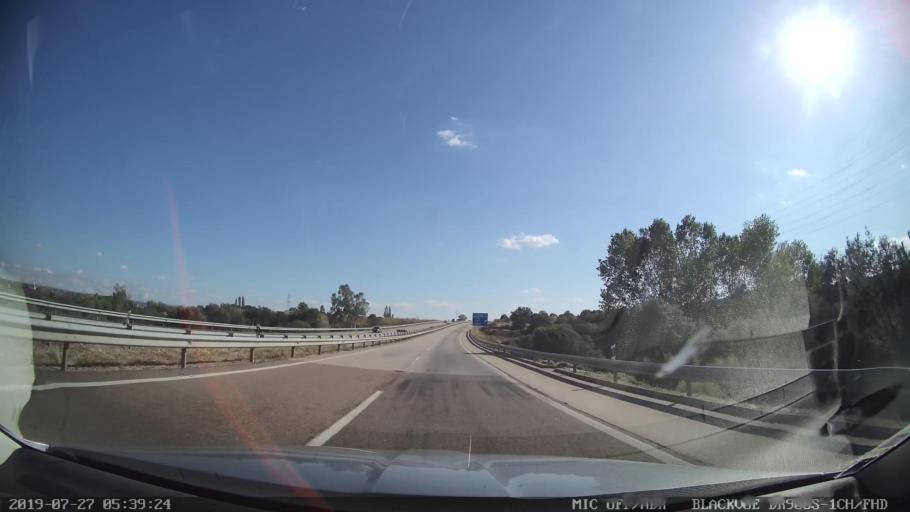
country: ES
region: Castille-La Mancha
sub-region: Province of Toledo
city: Talavera de la Reina
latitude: 39.9932
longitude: -4.8367
